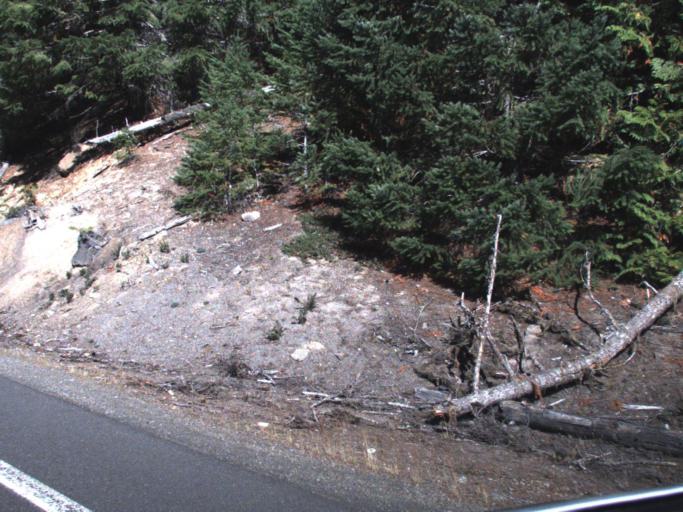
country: US
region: Washington
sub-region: Yakima County
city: Tieton
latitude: 46.6385
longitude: -121.4530
